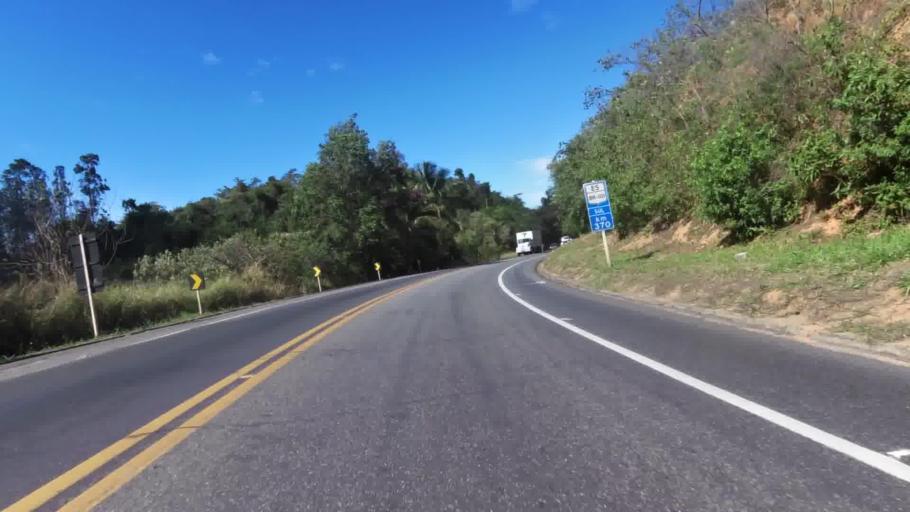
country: BR
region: Espirito Santo
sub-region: Iconha
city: Iconha
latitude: -20.7670
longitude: -40.7597
